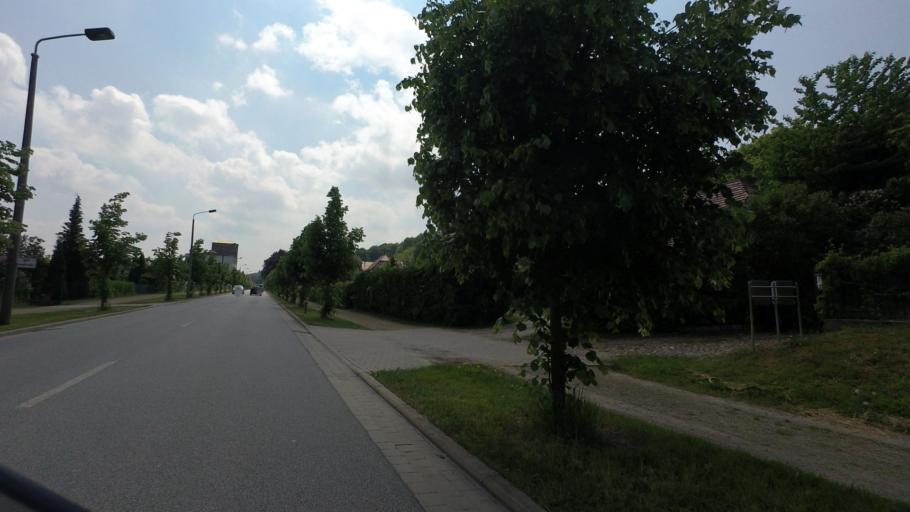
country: DE
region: Brandenburg
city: Spremberg
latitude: 51.5797
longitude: 14.3619
